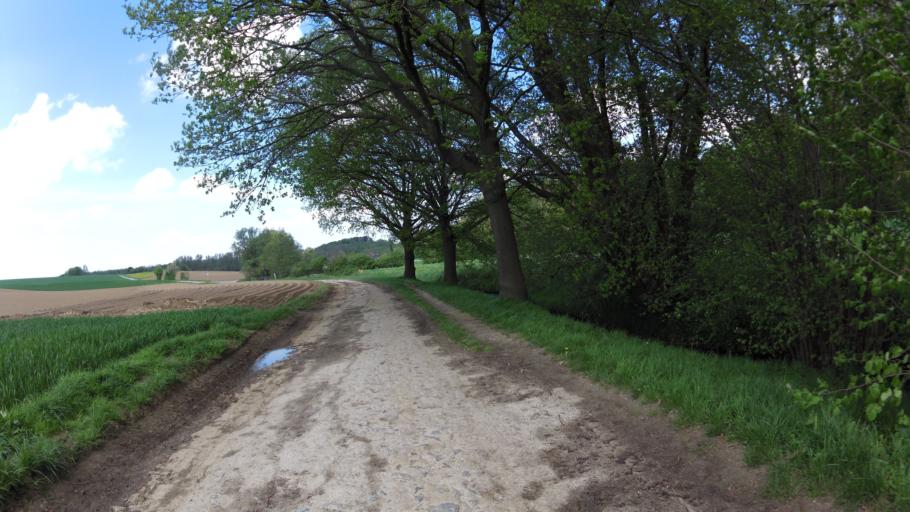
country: NL
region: Limburg
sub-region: Gemeente Kerkrade
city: Kerkrade
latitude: 50.8501
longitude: 6.0563
